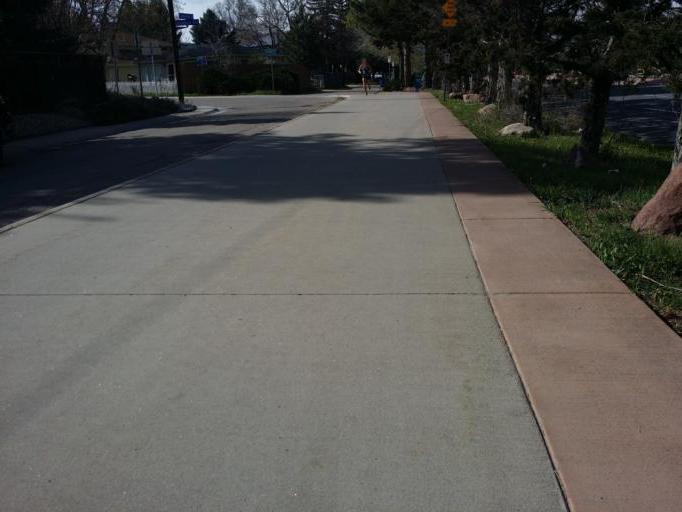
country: US
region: Colorado
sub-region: Boulder County
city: Boulder
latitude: 39.9989
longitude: -105.2631
